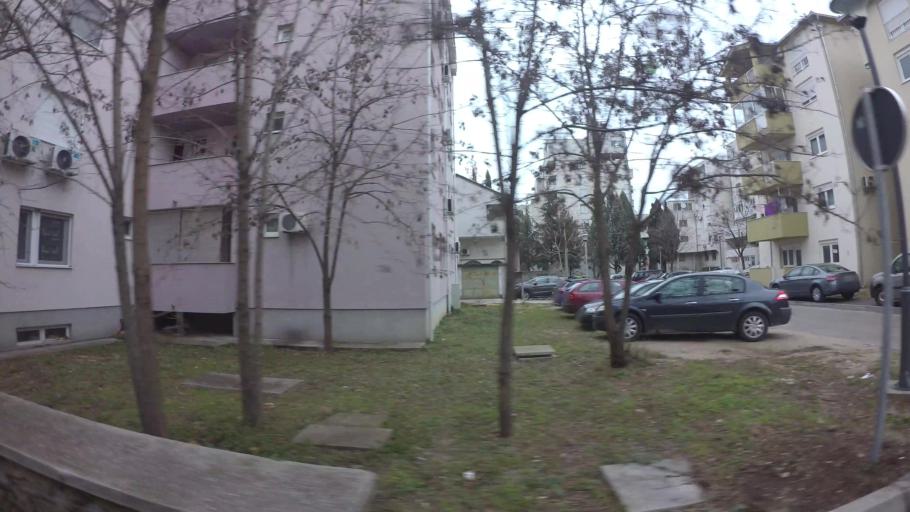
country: BA
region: Federation of Bosnia and Herzegovina
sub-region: Hercegovacko-Bosanski Kanton
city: Mostar
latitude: 43.3409
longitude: 17.8089
